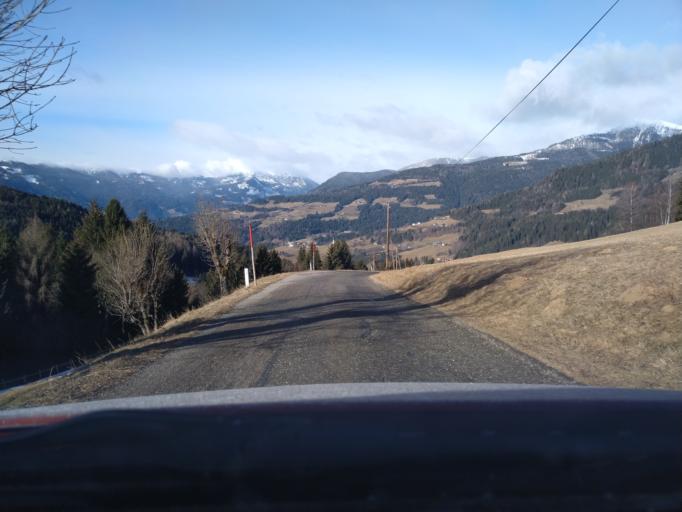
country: AT
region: Carinthia
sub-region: Politischer Bezirk Villach Land
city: Arriach
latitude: 46.7198
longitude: 13.8839
